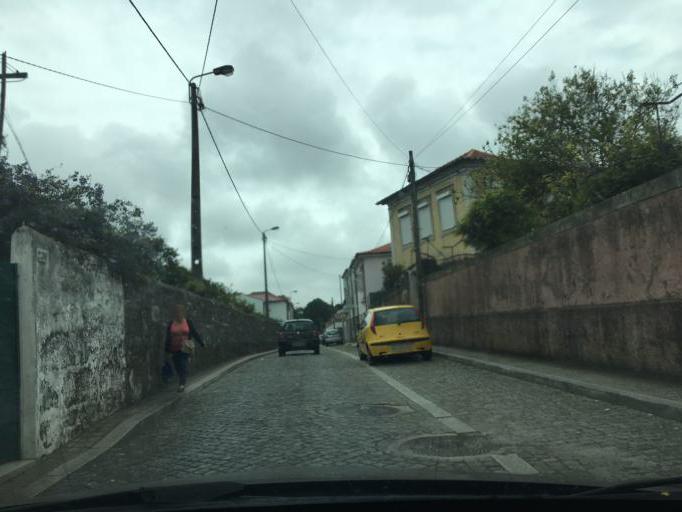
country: PT
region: Porto
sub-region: Matosinhos
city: Santa Cruz do Bispo
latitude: 41.2202
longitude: -8.6767
